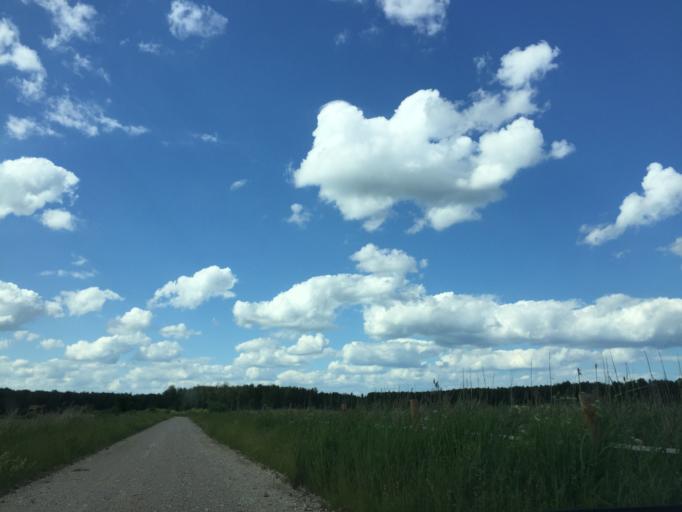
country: LV
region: Engure
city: Smarde
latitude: 56.8674
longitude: 23.3872
